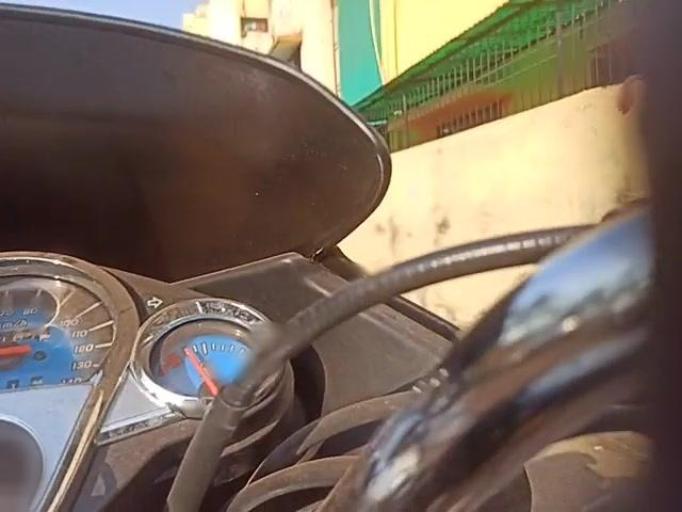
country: IN
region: Chhattisgarh
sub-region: Durg
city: Durg
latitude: 21.2143
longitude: 81.3070
